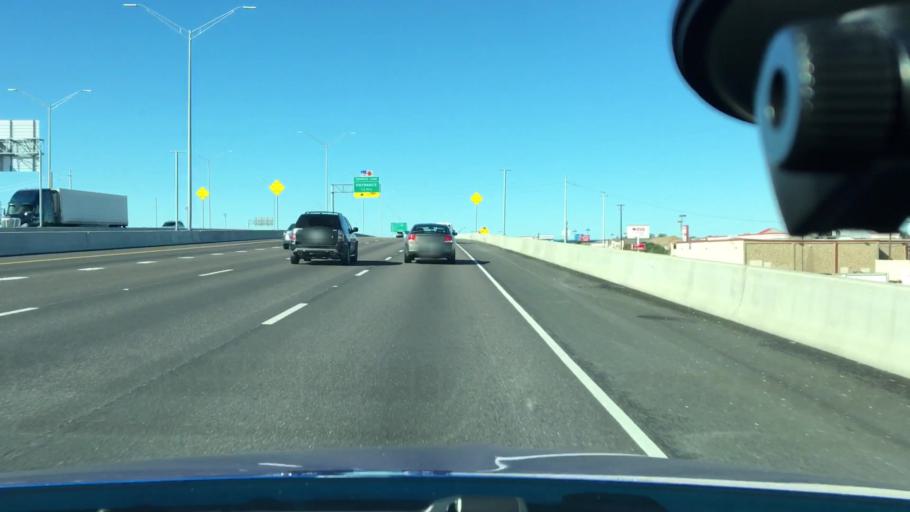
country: US
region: Texas
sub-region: Dallas County
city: Irving
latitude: 32.8375
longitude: -96.9736
